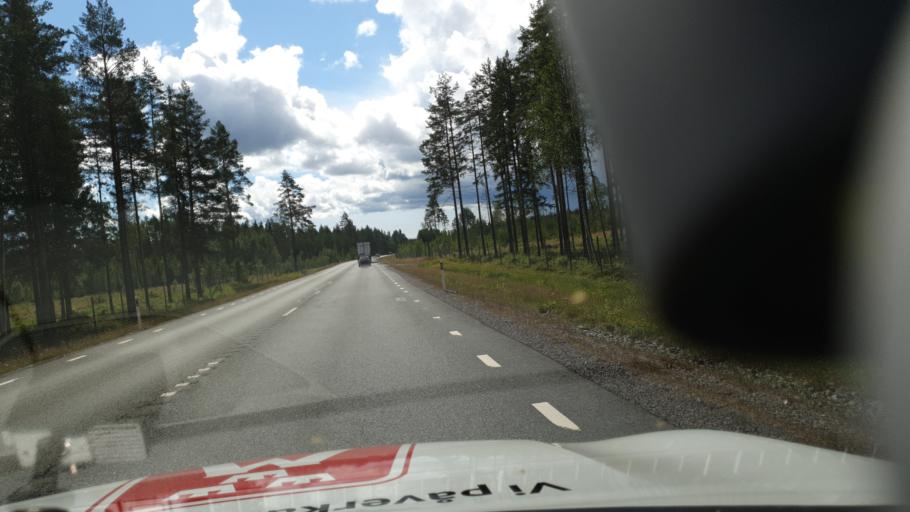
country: SE
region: Vaesterbotten
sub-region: Skelleftea Kommun
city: Burea
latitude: 64.5249
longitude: 21.2585
